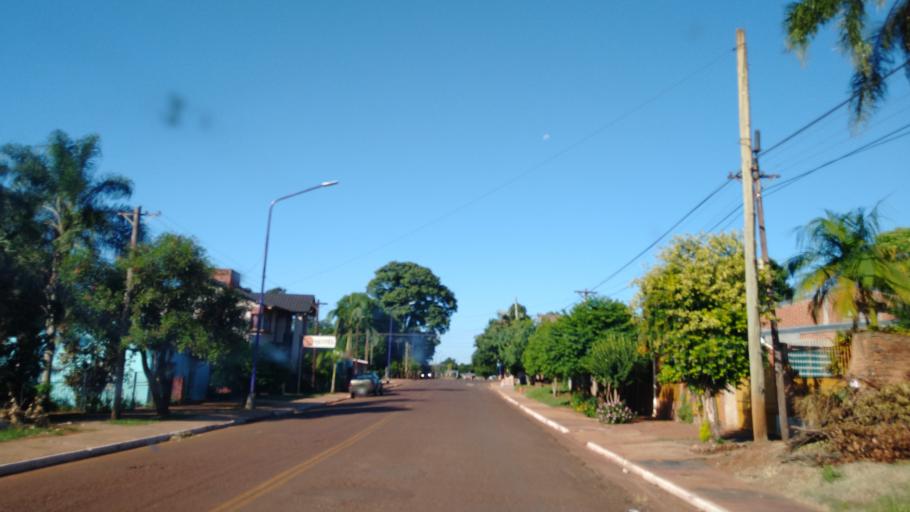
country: AR
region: Misiones
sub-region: Departamento de San Ignacio
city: San Ignacio
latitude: -27.2518
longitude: -55.5324
